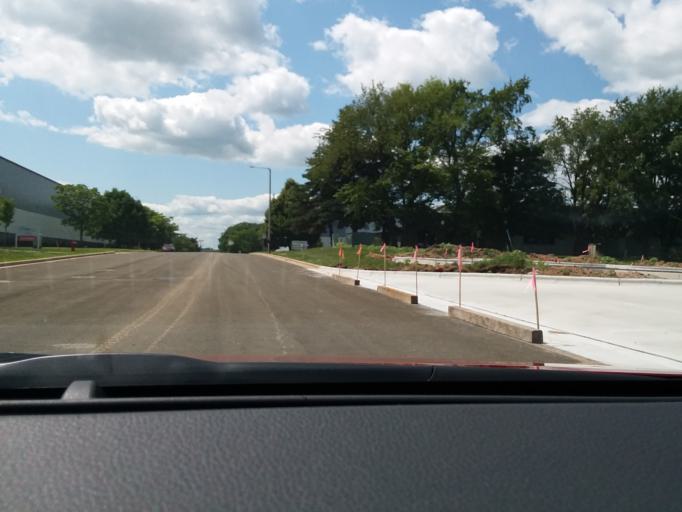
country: US
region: Wisconsin
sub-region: Dane County
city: Windsor
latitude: 43.1998
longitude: -89.3376
